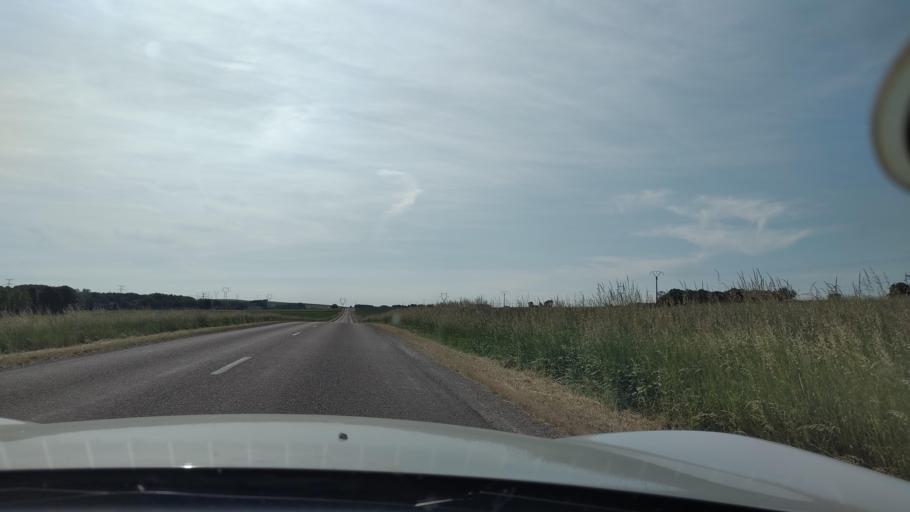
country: FR
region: Champagne-Ardenne
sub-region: Departement de l'Aube
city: Nogent-sur-Seine
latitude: 48.4653
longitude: 3.5743
